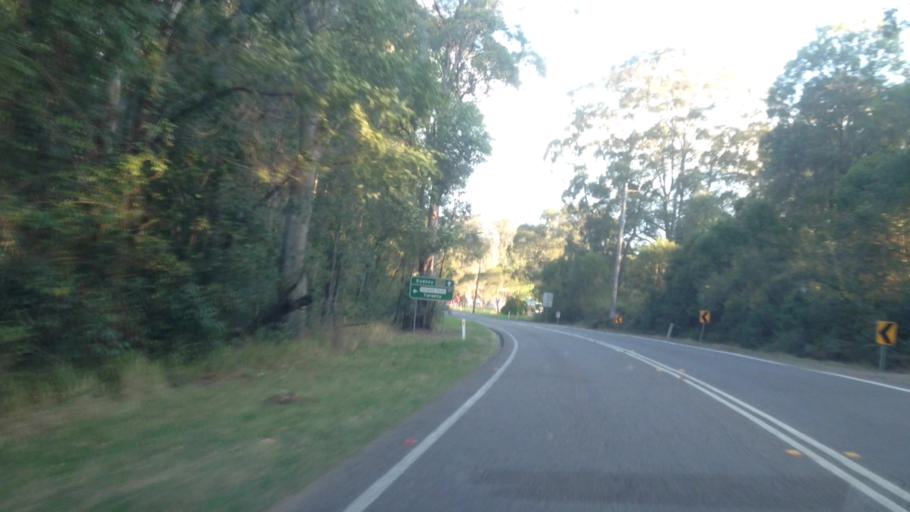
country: AU
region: New South Wales
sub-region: Lake Macquarie Shire
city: Cooranbong
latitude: -32.9817
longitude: 151.4841
